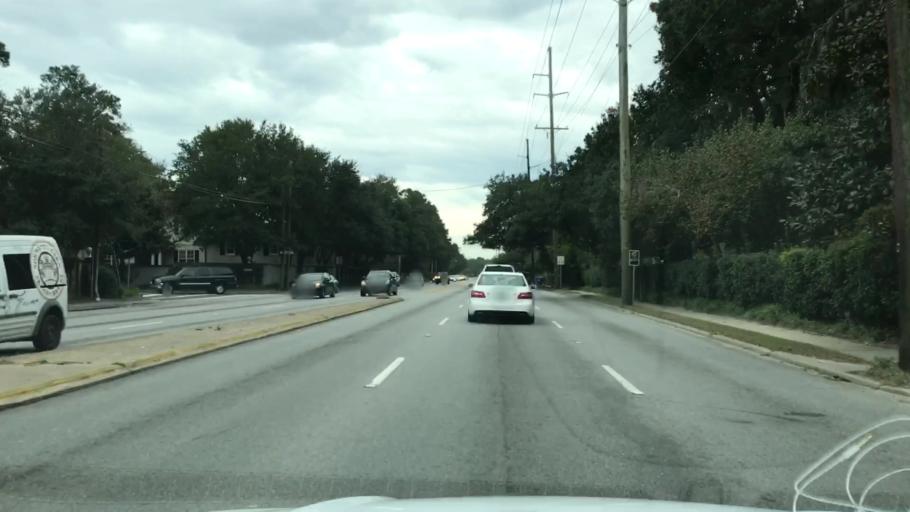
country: US
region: South Carolina
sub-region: Charleston County
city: Charleston
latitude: 32.7743
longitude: -79.9738
